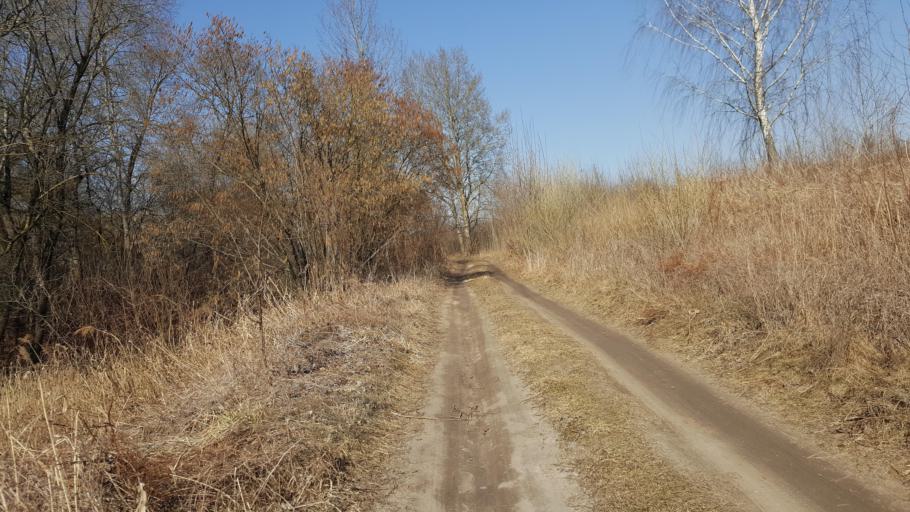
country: BY
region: Brest
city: Kamyanyets
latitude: 52.3633
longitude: 23.7447
